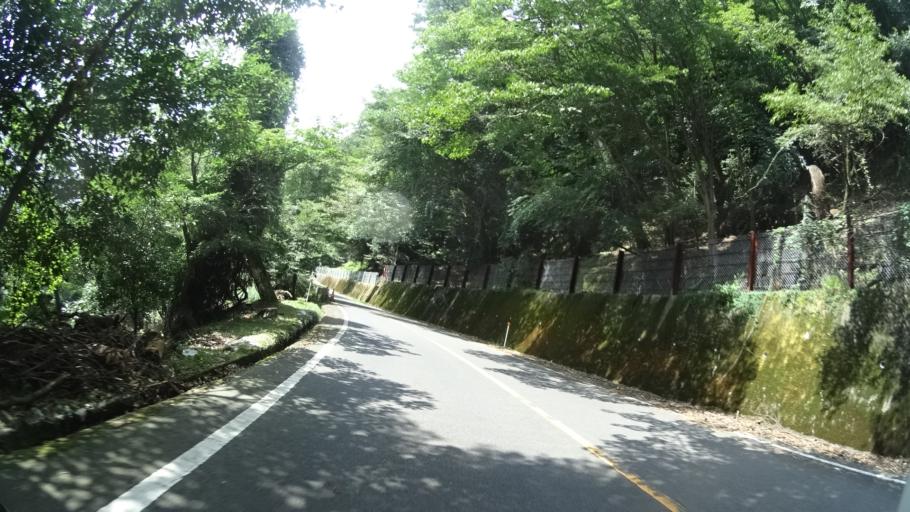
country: JP
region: Miyazaki
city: Kobayashi
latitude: 31.9014
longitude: 130.8419
